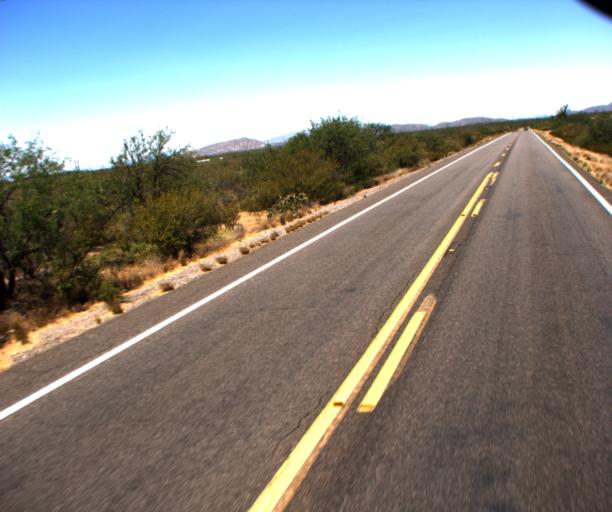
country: US
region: Arizona
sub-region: Pima County
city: Catalina
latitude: 32.6557
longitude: -111.0382
